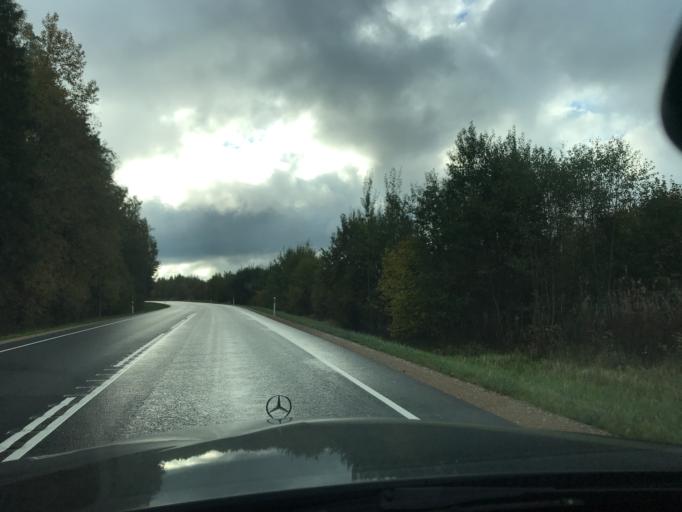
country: EE
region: Viljandimaa
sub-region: Karksi vald
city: Karksi-Nuia
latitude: 58.0571
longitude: 25.6306
